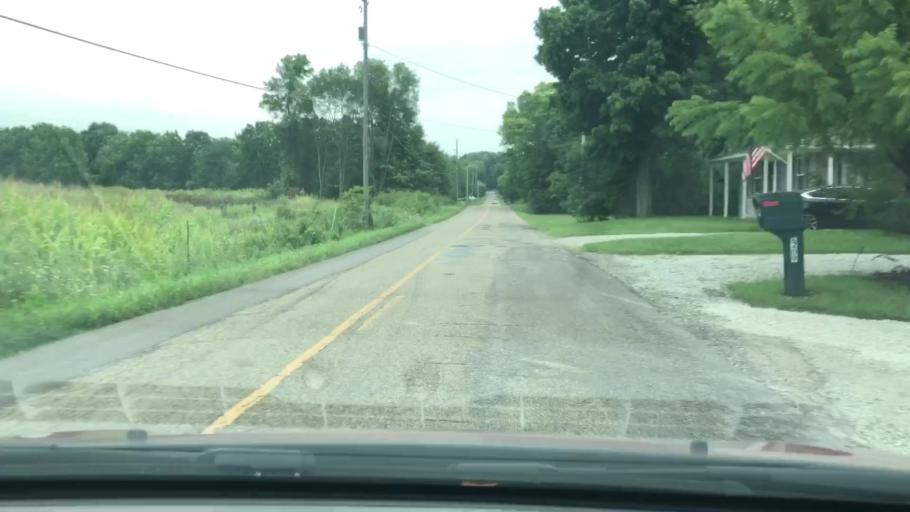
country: US
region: Ohio
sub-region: Knox County
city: Centerburg
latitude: 40.3160
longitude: -82.7259
